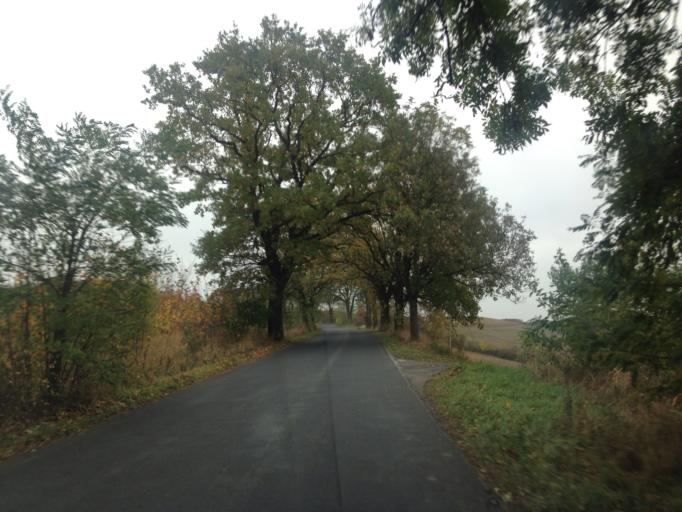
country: PL
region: Kujawsko-Pomorskie
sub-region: Grudziadz
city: Grudziadz
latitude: 53.3991
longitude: 18.8187
